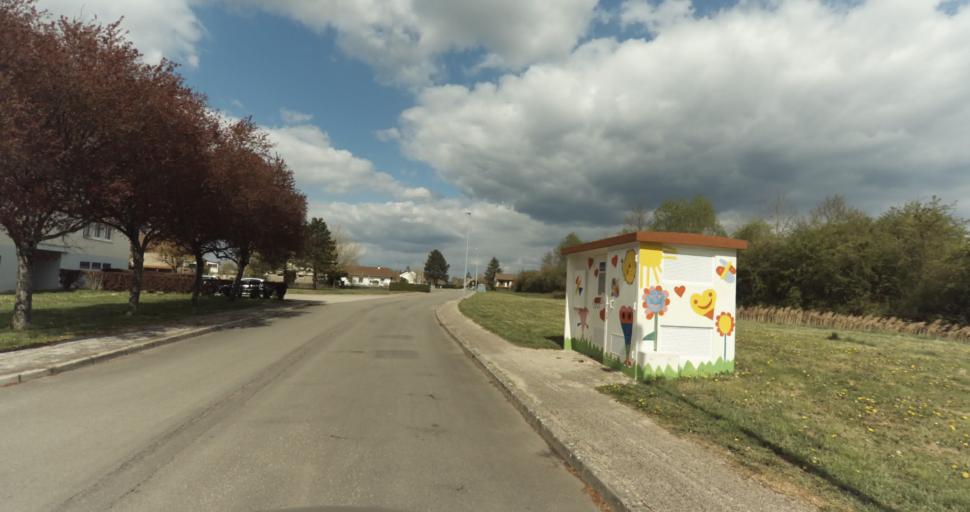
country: FR
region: Bourgogne
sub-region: Departement de la Cote-d'Or
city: Auxonne
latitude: 47.1928
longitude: 5.4103
